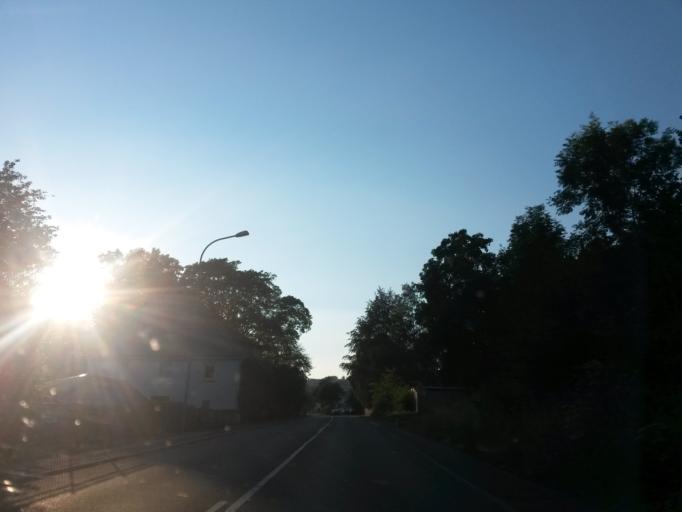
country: DE
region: North Rhine-Westphalia
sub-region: Regierungsbezirk Arnsberg
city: Herscheid
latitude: 51.1744
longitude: 7.7545
